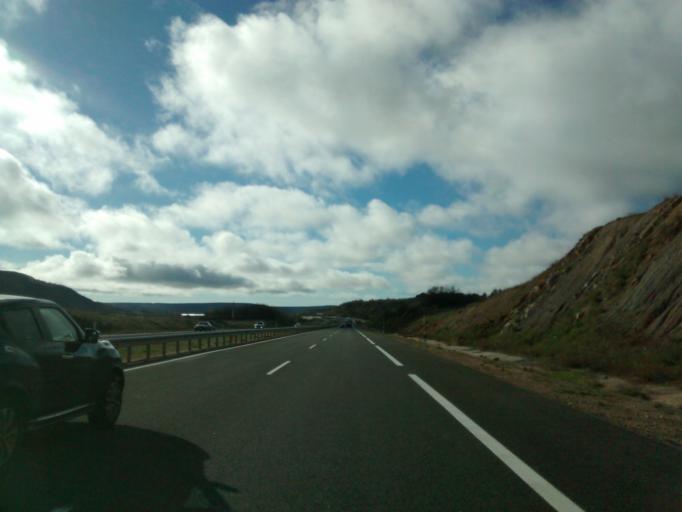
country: ES
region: Cantabria
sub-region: Provincia de Cantabria
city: Mataporquera
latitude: 42.8305
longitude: -4.2005
